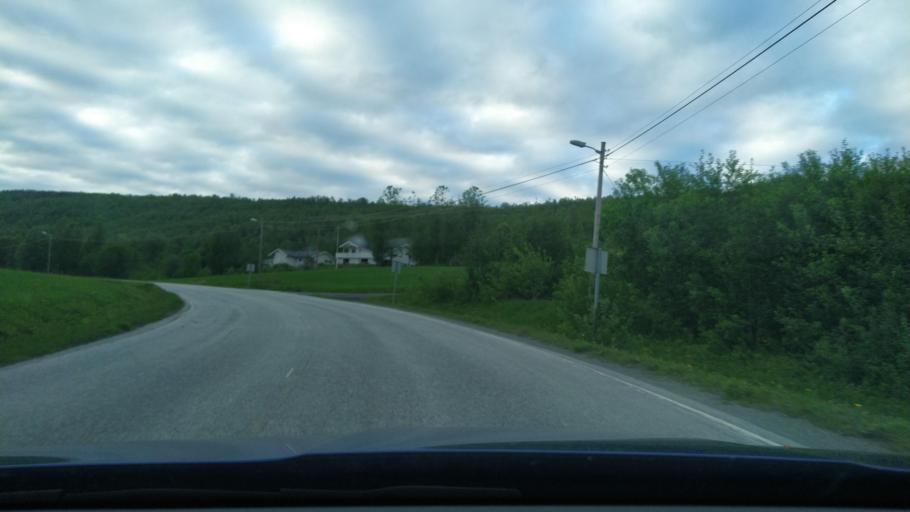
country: NO
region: Troms
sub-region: Sorreisa
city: Sorreisa
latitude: 69.1209
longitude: 18.2204
